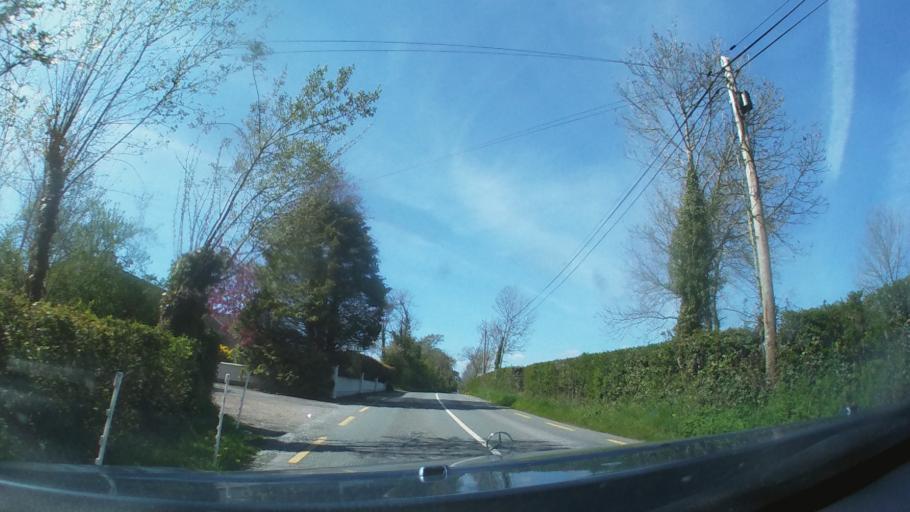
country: IE
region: Leinster
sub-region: Kilkenny
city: Kilkenny
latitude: 52.6411
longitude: -7.3059
